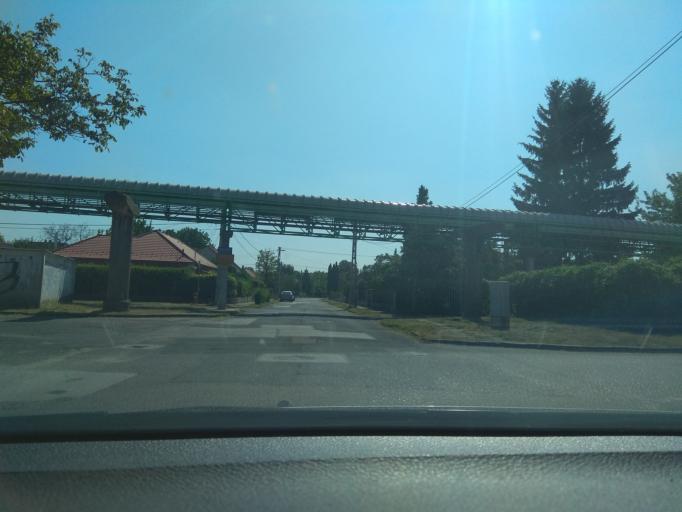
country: HU
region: Borsod-Abauj-Zemplen
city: Miskolc
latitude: 48.0657
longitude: 20.7869
